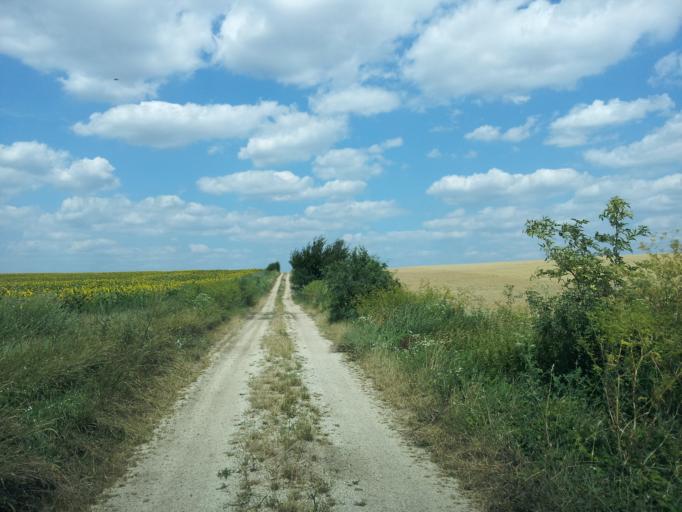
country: HU
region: Veszprem
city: Balatonkenese
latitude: 47.0529
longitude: 18.0760
